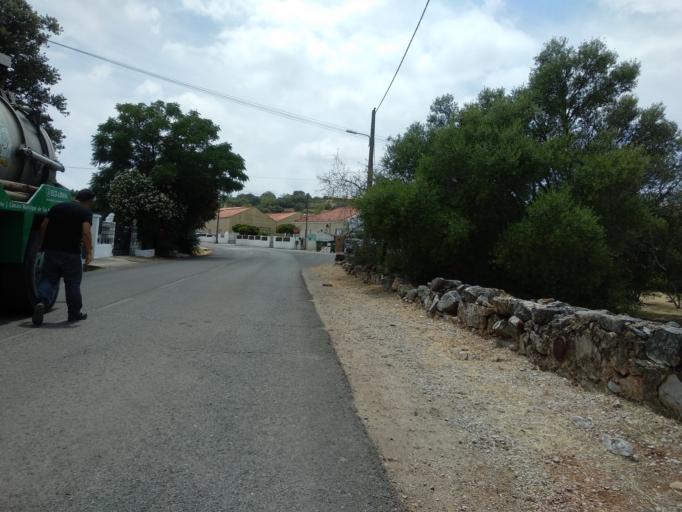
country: PT
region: Faro
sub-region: Sao Bras de Alportel
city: Sao Bras de Alportel
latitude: 37.1662
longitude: -7.8920
